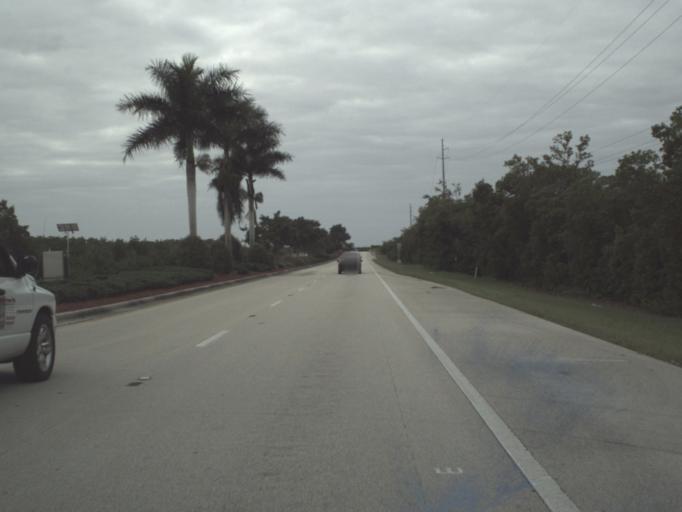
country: US
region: Florida
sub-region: Collier County
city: Marco
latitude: 25.9920
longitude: -81.7022
